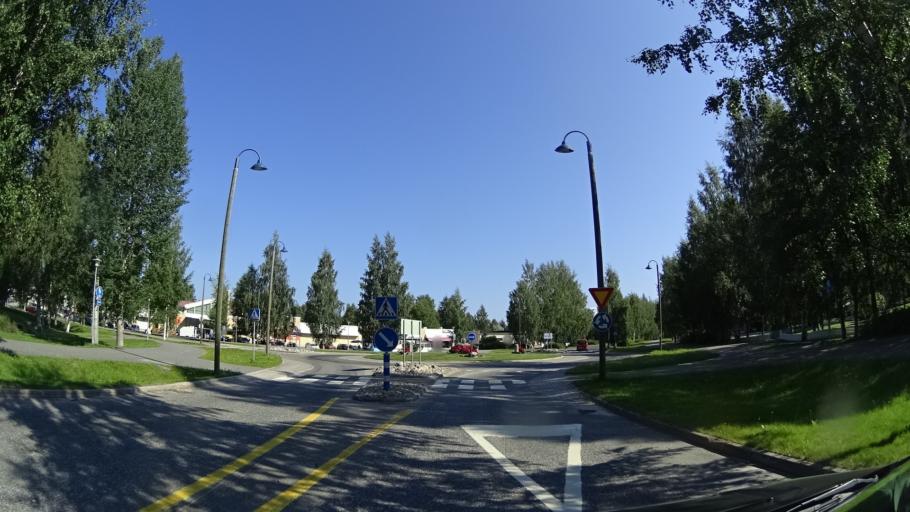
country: FI
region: North Karelia
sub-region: Joensuu
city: Juuka
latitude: 63.2427
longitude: 29.2539
